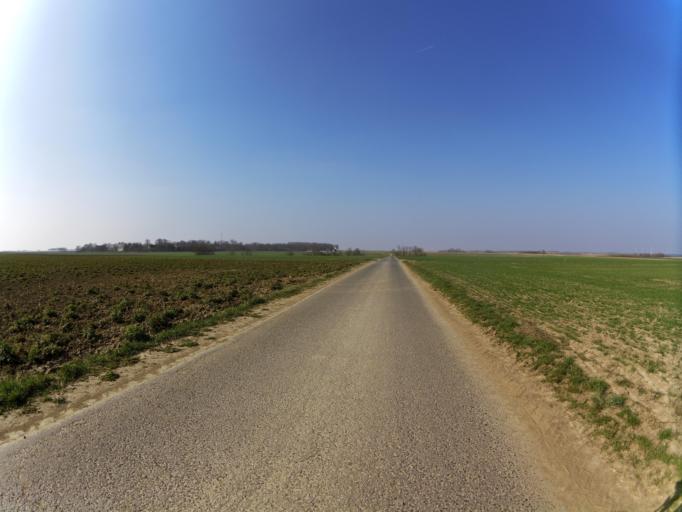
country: DE
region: Bavaria
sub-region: Regierungsbezirk Unterfranken
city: Gaukonigshofen
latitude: 49.6500
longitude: 9.9919
